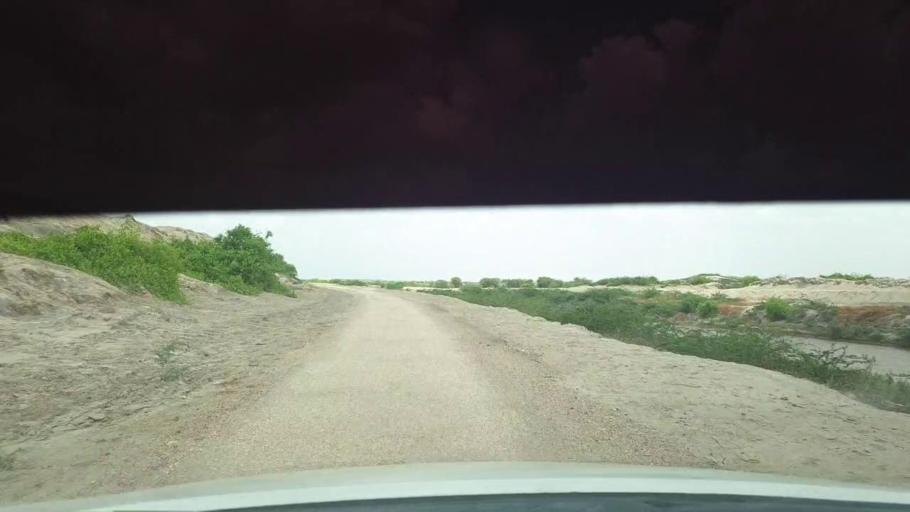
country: PK
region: Sindh
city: Kadhan
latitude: 24.5062
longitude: 69.1175
